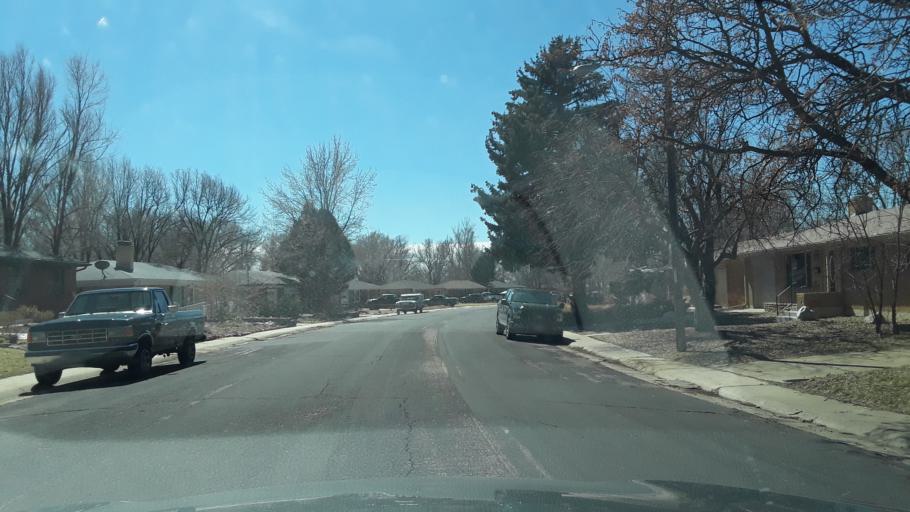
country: US
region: Colorado
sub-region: El Paso County
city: Colorado Springs
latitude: 38.8775
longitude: -104.7976
